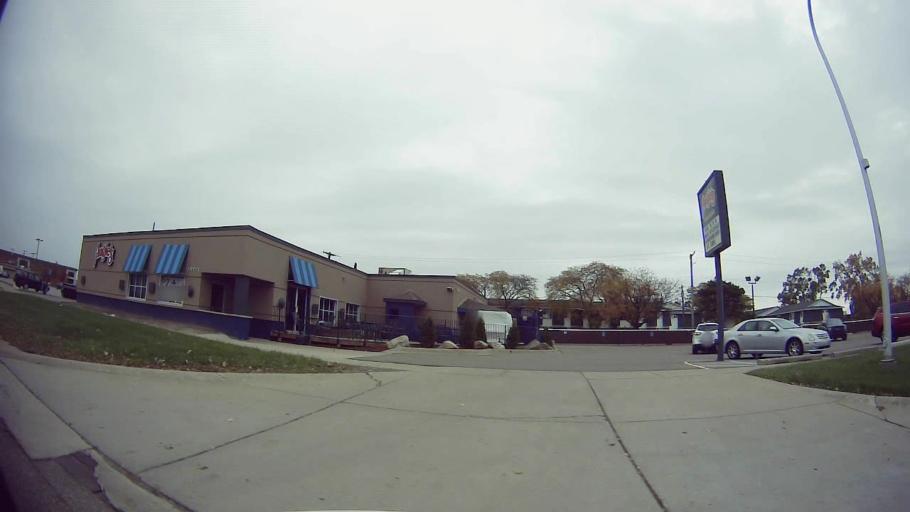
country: US
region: Michigan
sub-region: Oakland County
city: Madison Heights
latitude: 42.5257
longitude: -83.1066
